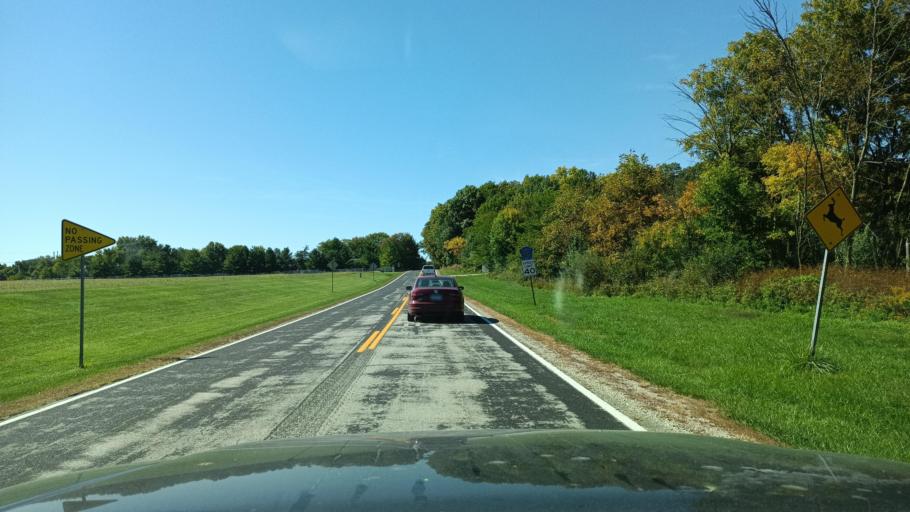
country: US
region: Illinois
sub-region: Champaign County
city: Lake of the Woods
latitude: 40.2077
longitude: -88.3655
